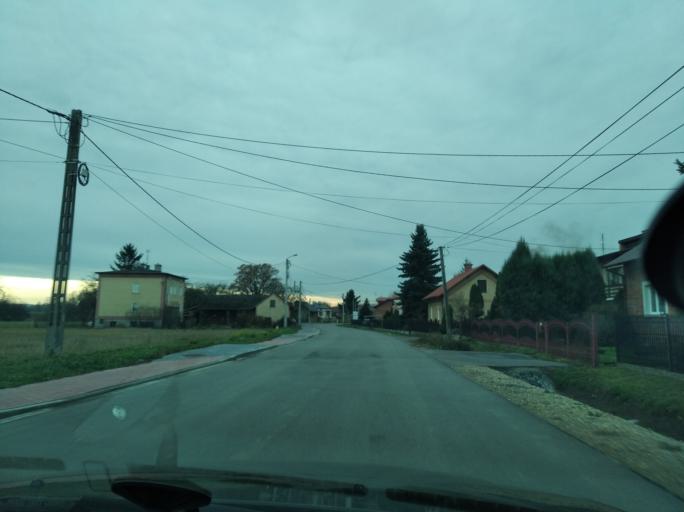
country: PL
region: Subcarpathian Voivodeship
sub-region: Powiat lancucki
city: Czarna
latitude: 50.0959
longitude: 22.1962
